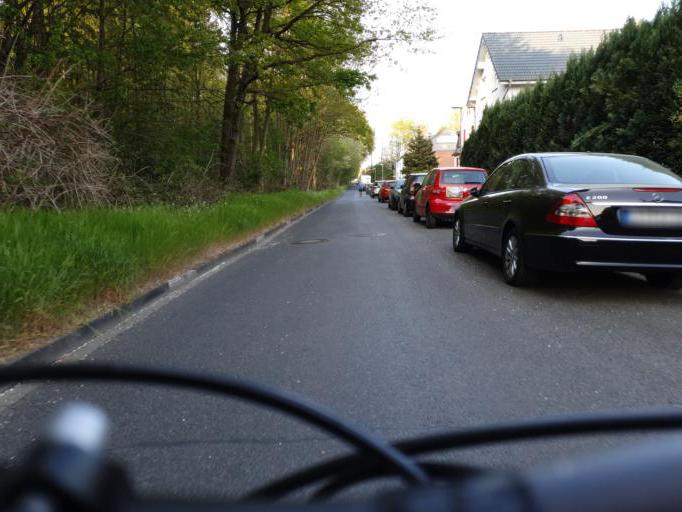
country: DE
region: North Rhine-Westphalia
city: Opladen
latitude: 51.0443
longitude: 7.0434
